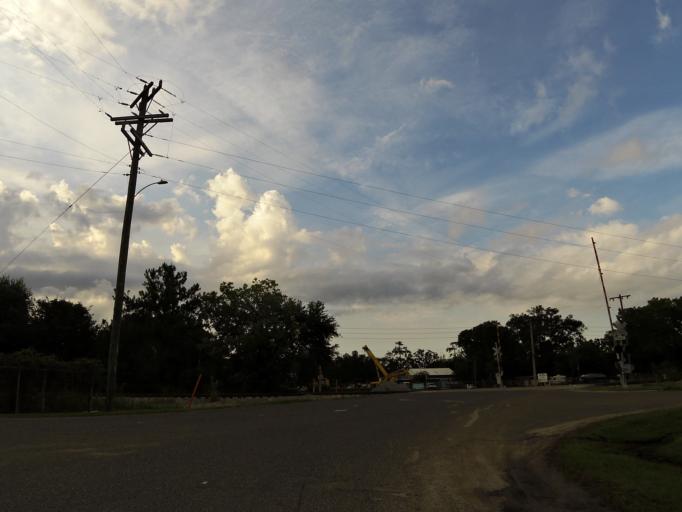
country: US
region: Florida
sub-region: Duval County
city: Jacksonville
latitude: 30.3222
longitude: -81.7667
